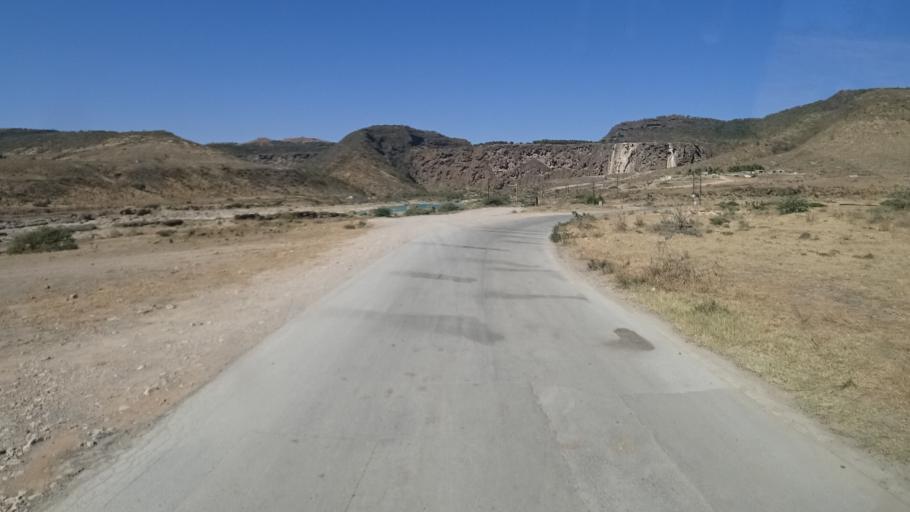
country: OM
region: Zufar
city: Salalah
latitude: 17.0661
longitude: 54.4311
